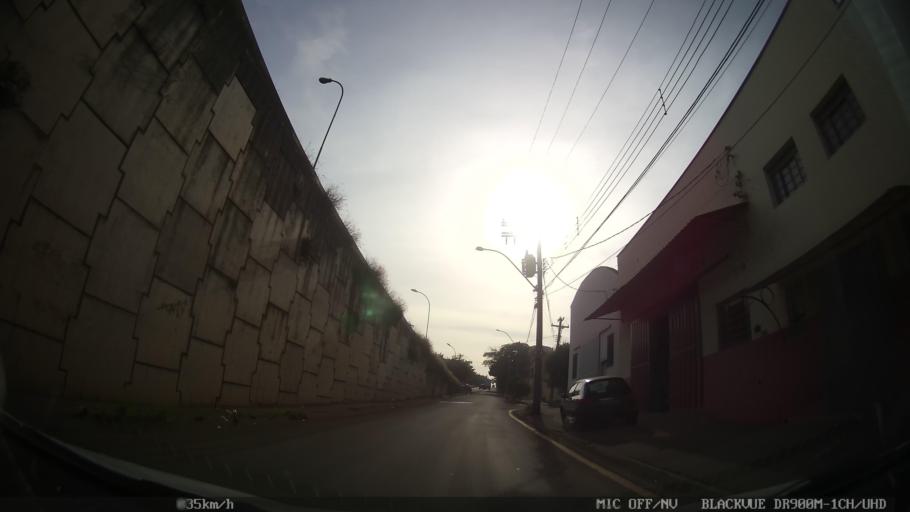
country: BR
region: Sao Paulo
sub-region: Piracicaba
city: Piracicaba
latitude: -22.7016
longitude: -47.6570
